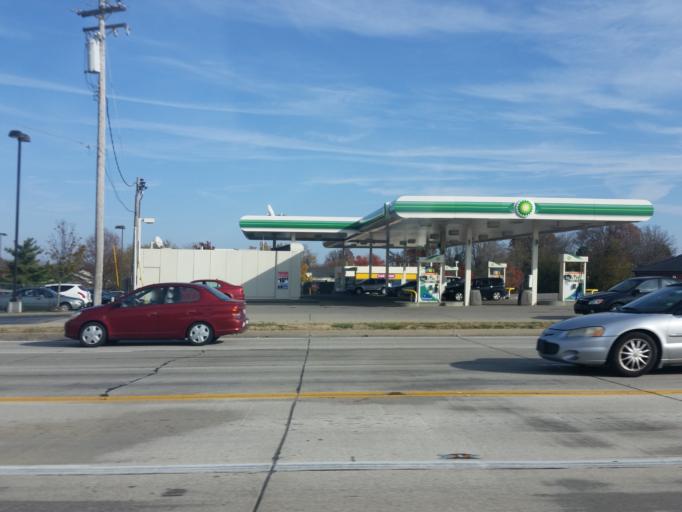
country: US
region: Kentucky
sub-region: Campbell County
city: Highland Heights
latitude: 39.0357
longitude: -84.4542
